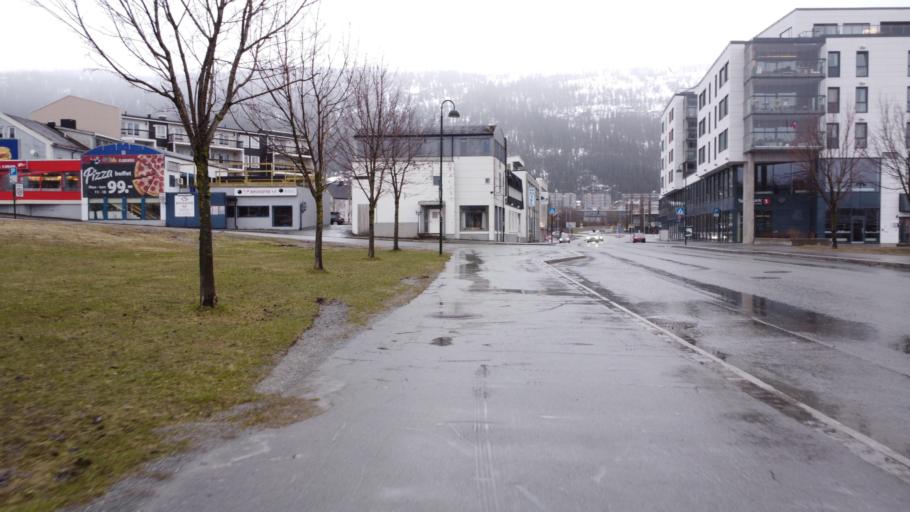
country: NO
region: Nordland
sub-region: Rana
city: Mo i Rana
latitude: 66.3088
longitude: 14.1355
